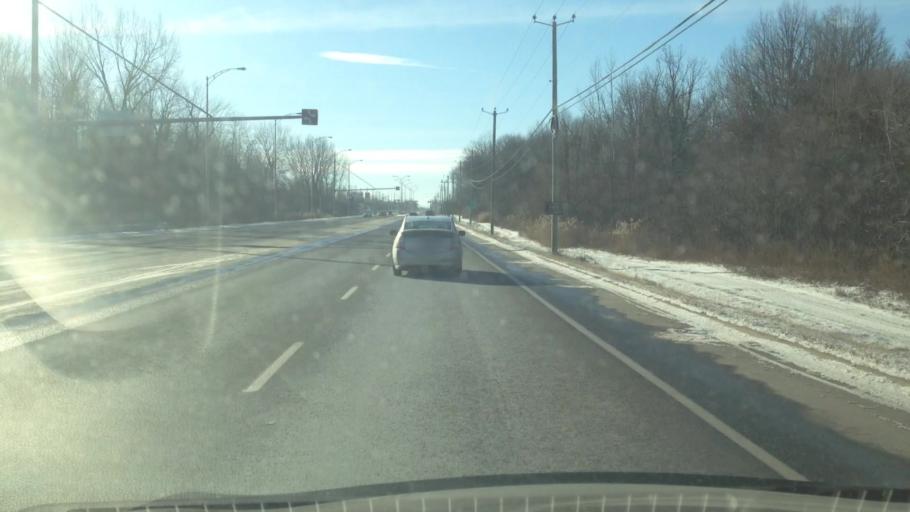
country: CA
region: Quebec
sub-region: Monteregie
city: Chateauguay
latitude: 45.3970
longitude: -73.6936
